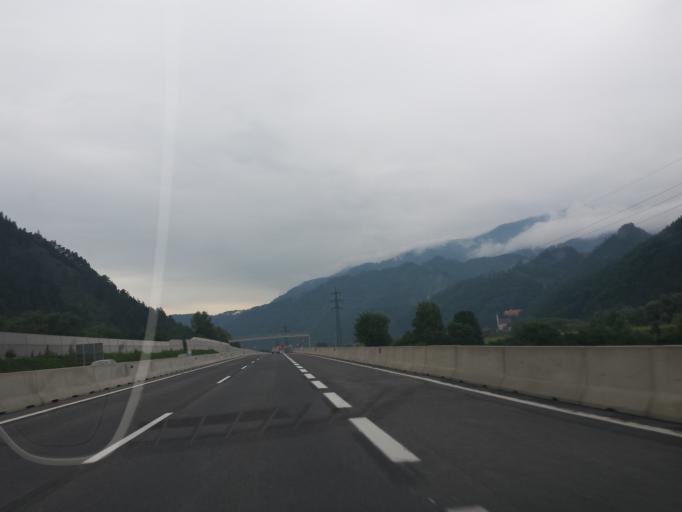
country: AT
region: Styria
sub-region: Politischer Bezirk Bruck-Muerzzuschlag
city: Pernegg an der Mur
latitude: 47.3457
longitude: 15.3474
